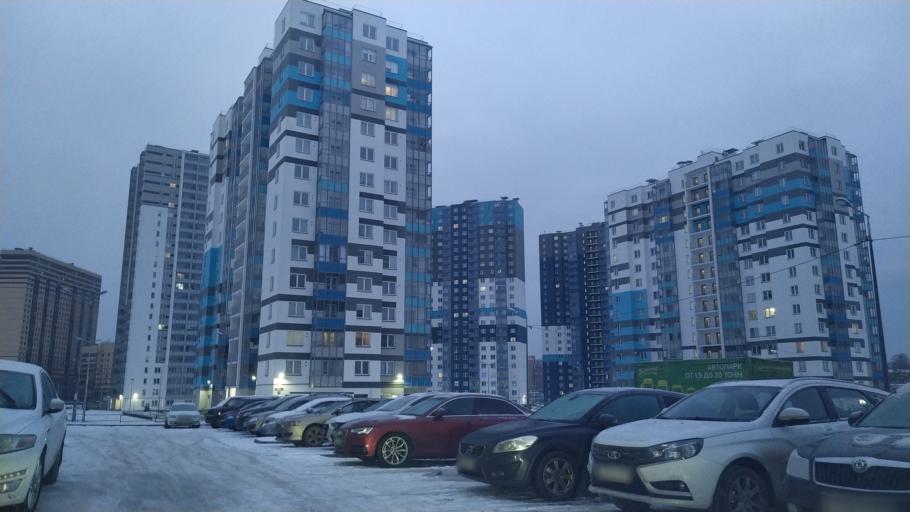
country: RU
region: Leningrad
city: Murino
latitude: 60.0347
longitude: 30.4555
